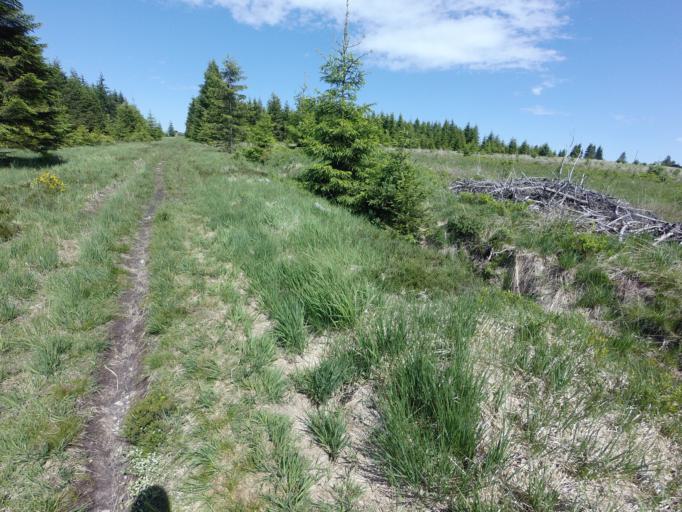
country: BE
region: Wallonia
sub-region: Province de Liege
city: Malmedy
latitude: 50.5114
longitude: 6.0395
